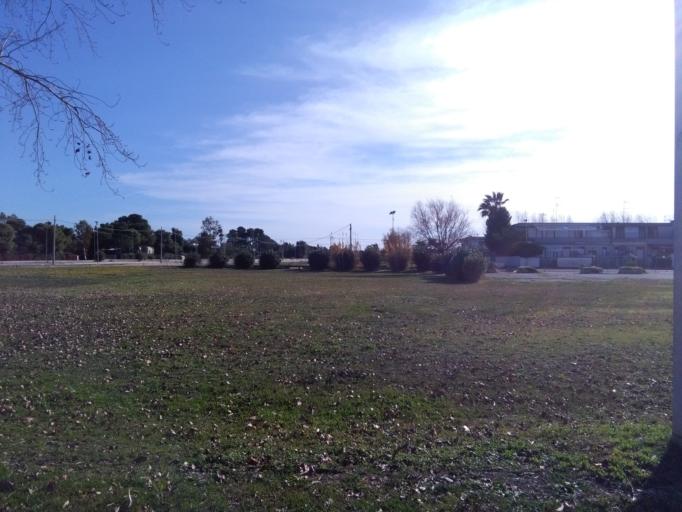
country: IT
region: Apulia
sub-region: Provincia di Foggia
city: Zapponeta
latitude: 41.5091
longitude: 15.9106
